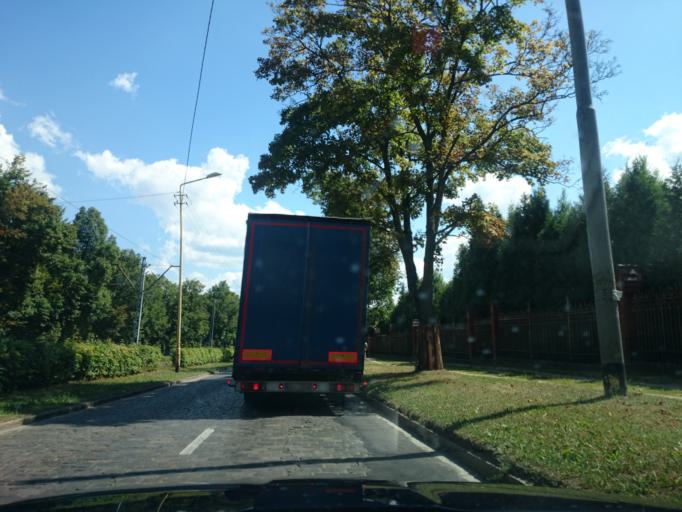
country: PL
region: West Pomeranian Voivodeship
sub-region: Szczecin
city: Szczecin
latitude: 53.4207
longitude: 14.5201
